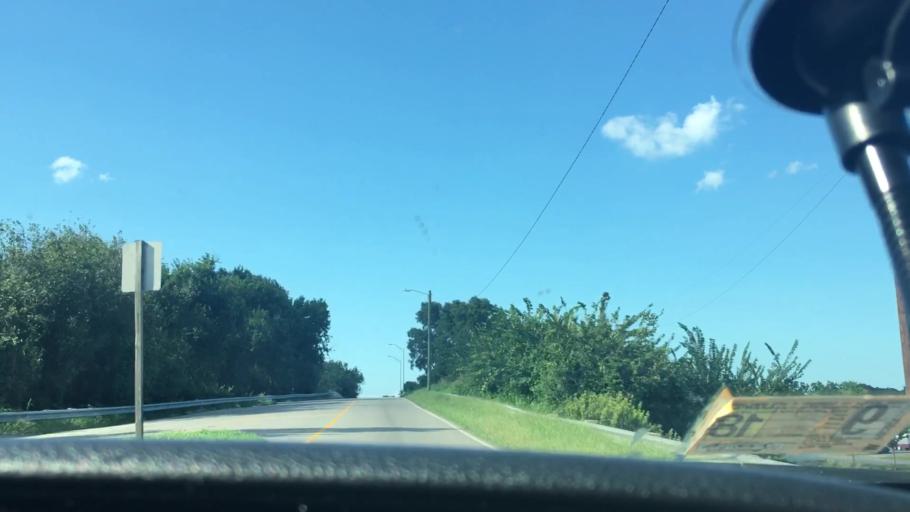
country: US
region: Virginia
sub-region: City of Chesapeake
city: Chesapeake
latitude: 36.8006
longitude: -76.2763
